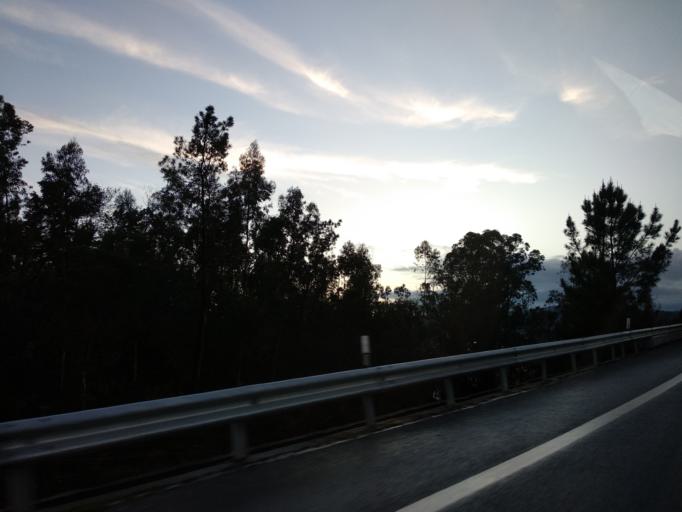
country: PT
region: Braga
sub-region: Braga
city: Oliveira
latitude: 41.5060
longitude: -8.4724
